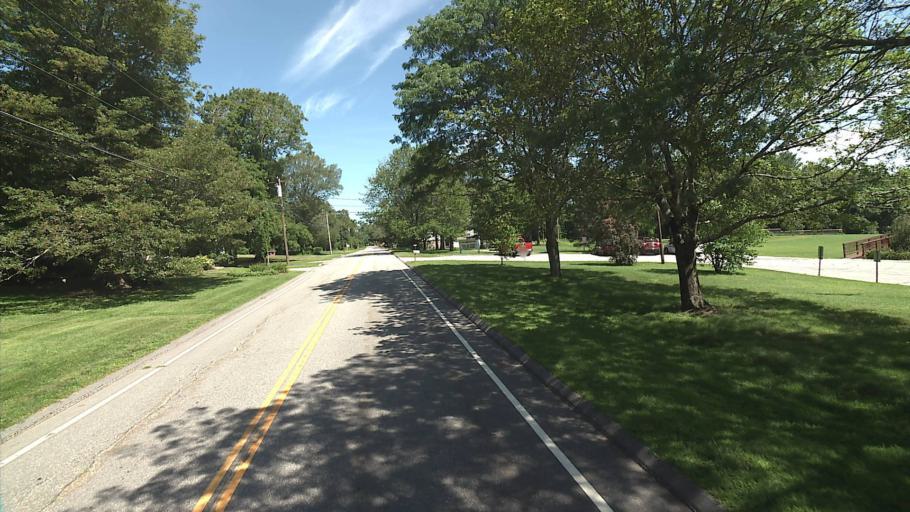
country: US
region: Connecticut
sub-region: Windham County
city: Windham
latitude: 41.7783
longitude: -72.0555
